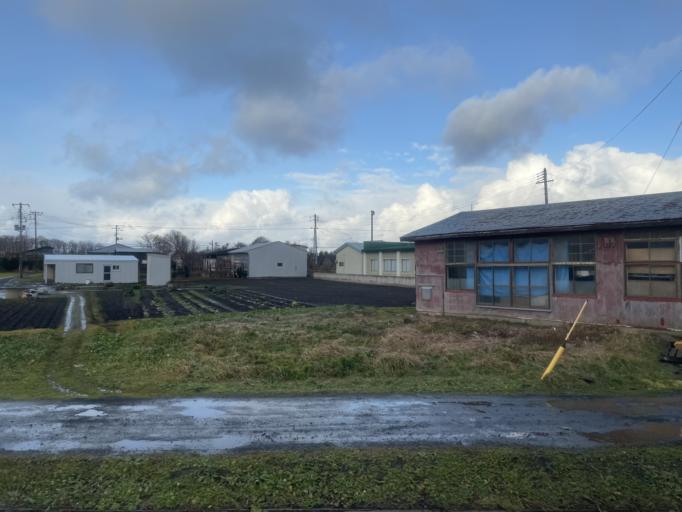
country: JP
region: Aomori
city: Misawa
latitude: 40.9167
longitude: 141.1916
